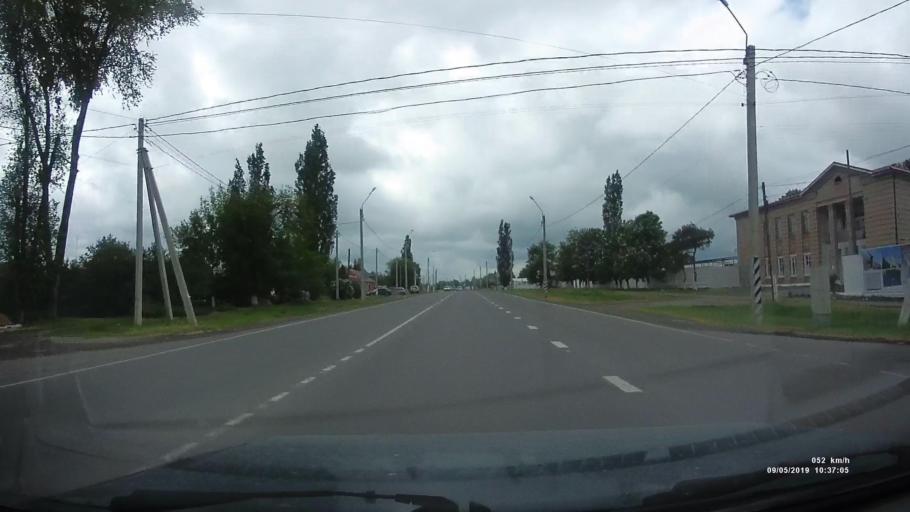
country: RU
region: Rostov
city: Peshkovo
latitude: 47.0232
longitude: 39.4046
